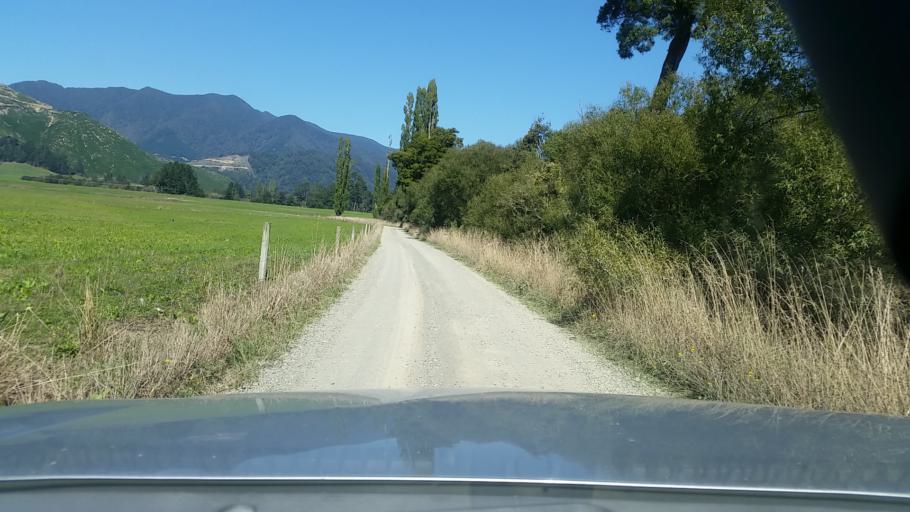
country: NZ
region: Nelson
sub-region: Nelson City
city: Nelson
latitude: -41.2670
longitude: 173.5758
